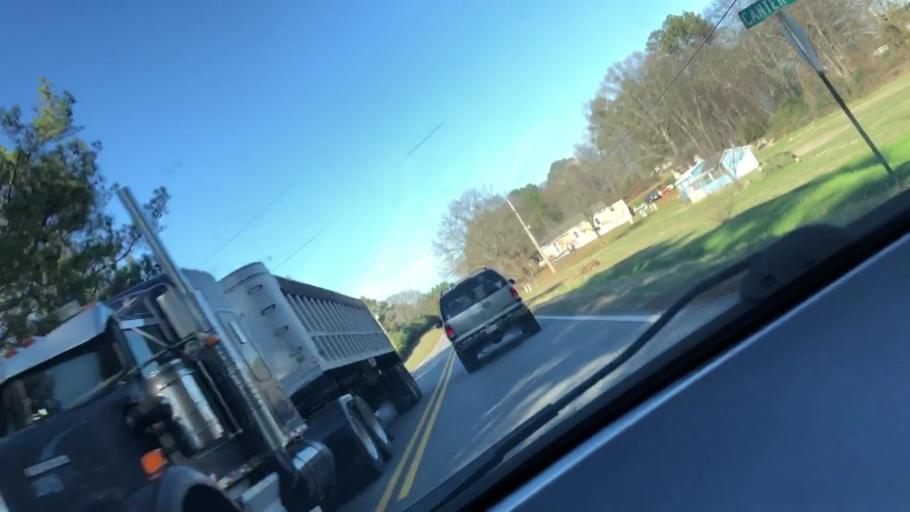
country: US
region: Georgia
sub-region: Bartow County
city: Cartersville
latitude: 34.2164
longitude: -84.8020
